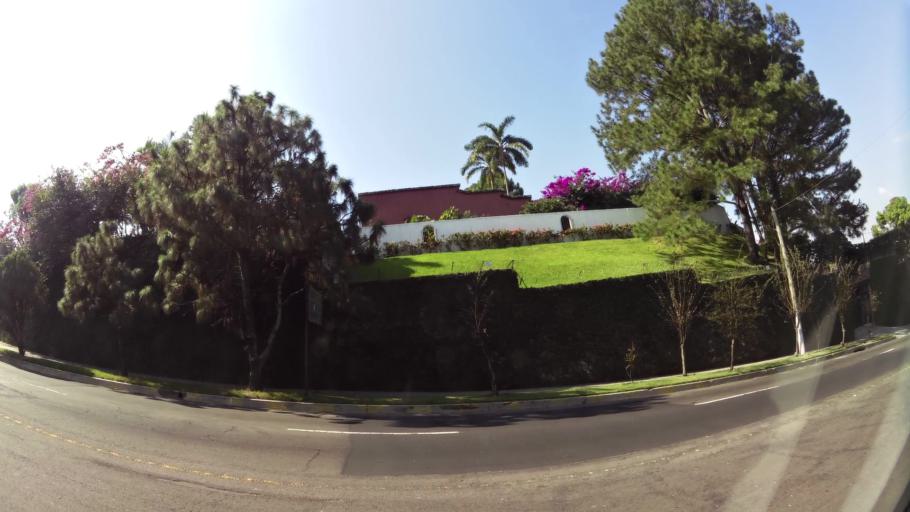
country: SV
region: La Libertad
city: Antiguo Cuscatlan
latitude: 13.6691
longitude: -89.2366
